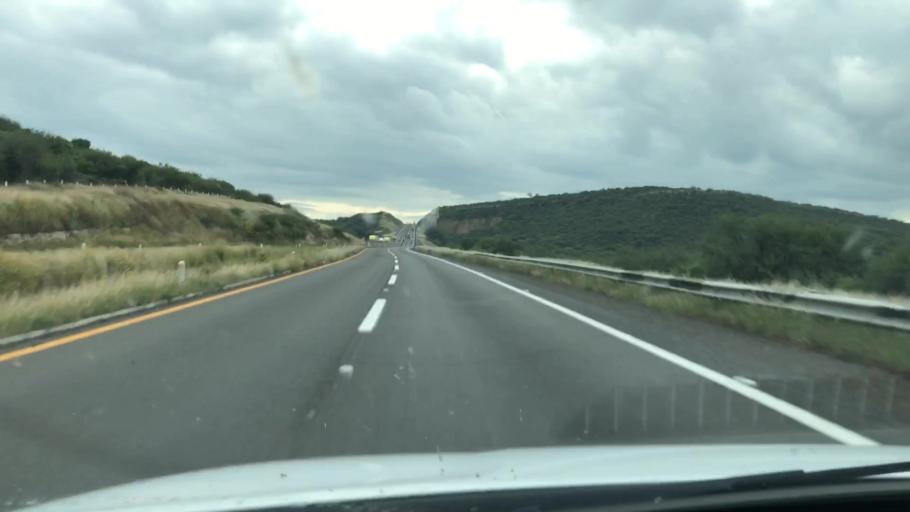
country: MX
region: Guanajuato
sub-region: Purisima del Rincon
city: Potrerillos (Guanajal)
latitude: 21.1434
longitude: -101.8373
